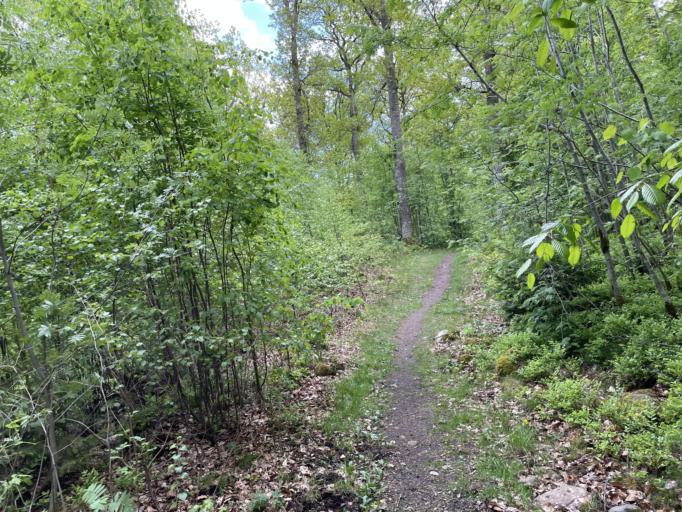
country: SE
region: Skane
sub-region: Klippans Kommun
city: Klippan
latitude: 56.1602
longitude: 13.1501
